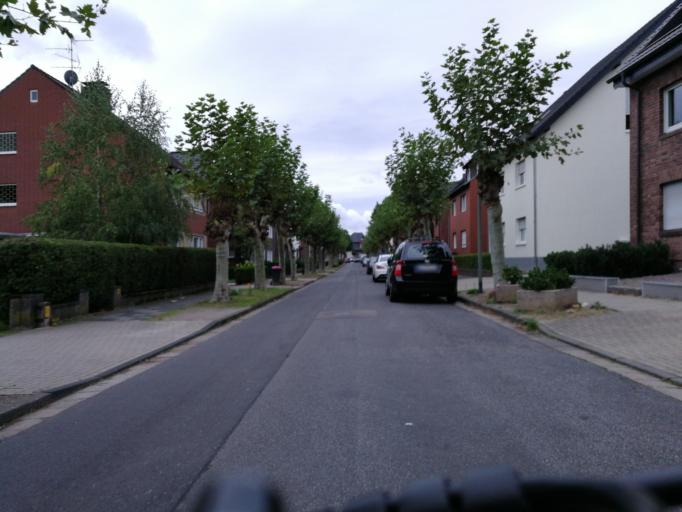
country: DE
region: North Rhine-Westphalia
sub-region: Regierungsbezirk Dusseldorf
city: Neuss
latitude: 51.1580
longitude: 6.7272
